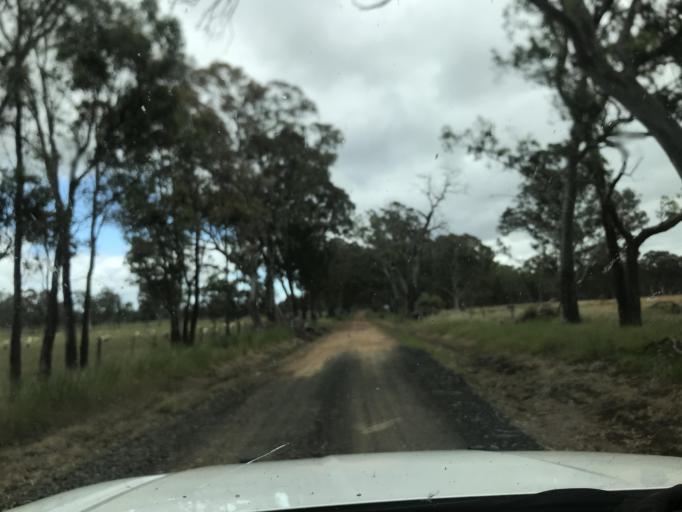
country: AU
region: South Australia
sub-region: Wattle Range
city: Penola
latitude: -37.1225
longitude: 141.2262
